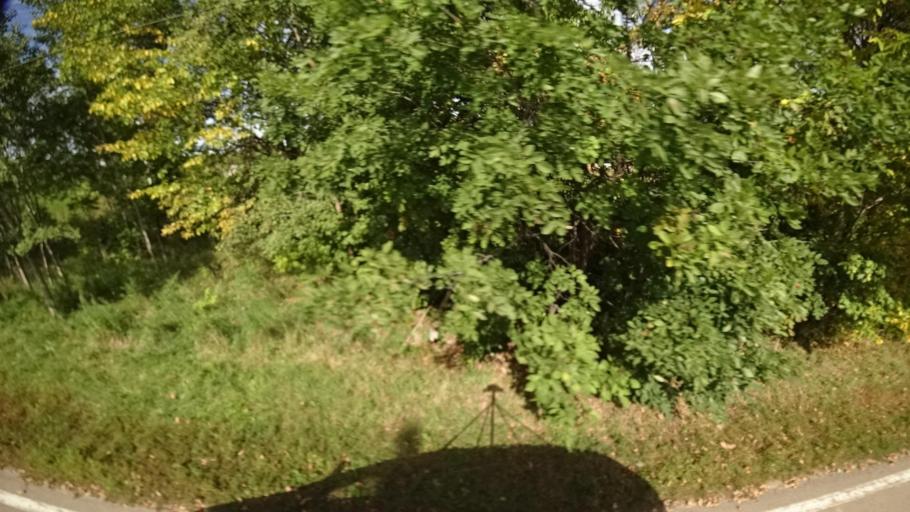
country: RU
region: Primorskiy
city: Yakovlevka
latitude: 44.3980
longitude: 133.5999
